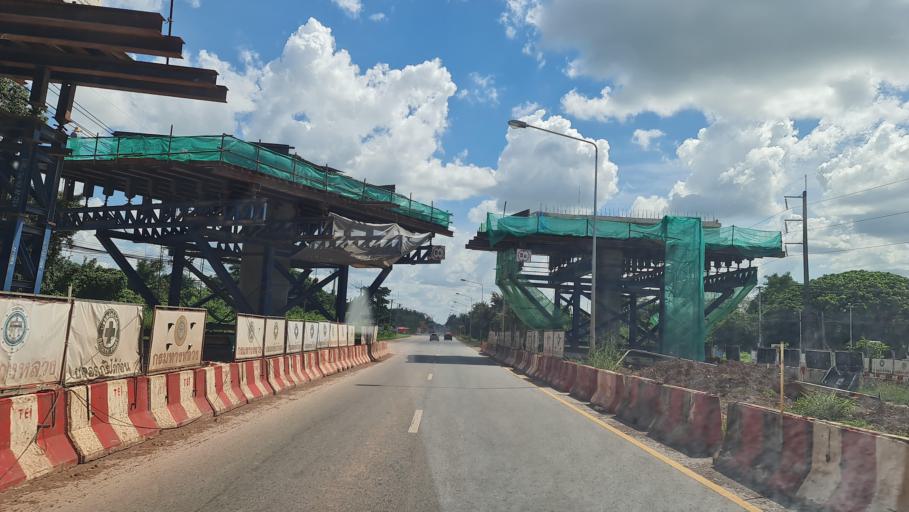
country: TH
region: Nong Khai
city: Nong Khai
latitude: 17.8012
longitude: 102.7616
